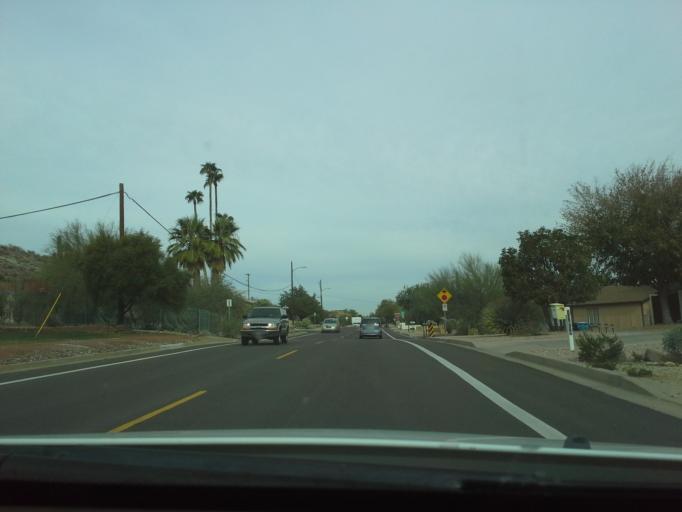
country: US
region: Arizona
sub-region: Maricopa County
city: Paradise Valley
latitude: 33.6099
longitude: -112.0219
